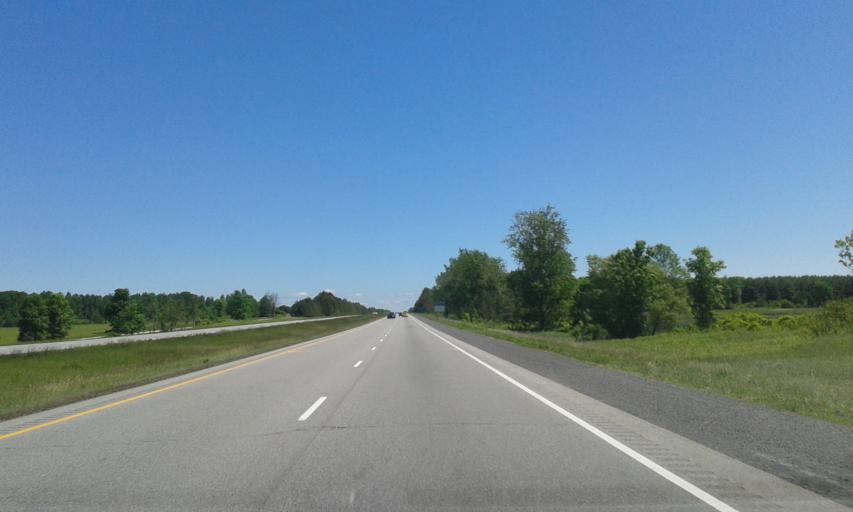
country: US
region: New York
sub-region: St. Lawrence County
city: Ogdensburg
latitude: 44.7979
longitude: -75.4246
